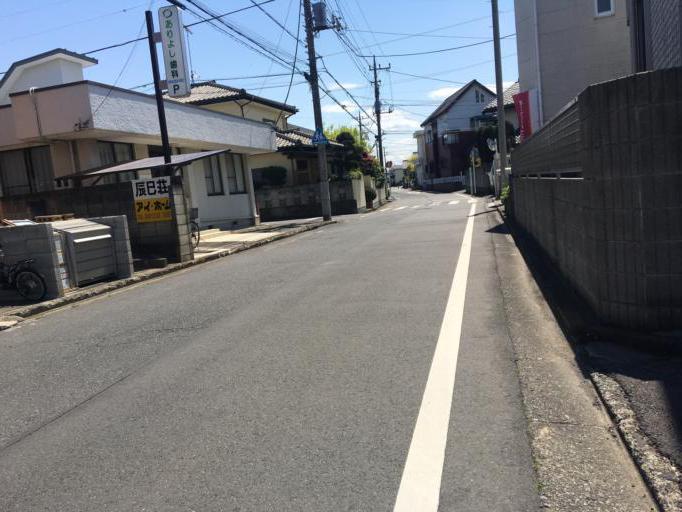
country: JP
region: Saitama
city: Kawagoe
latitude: 35.9279
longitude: 139.4446
